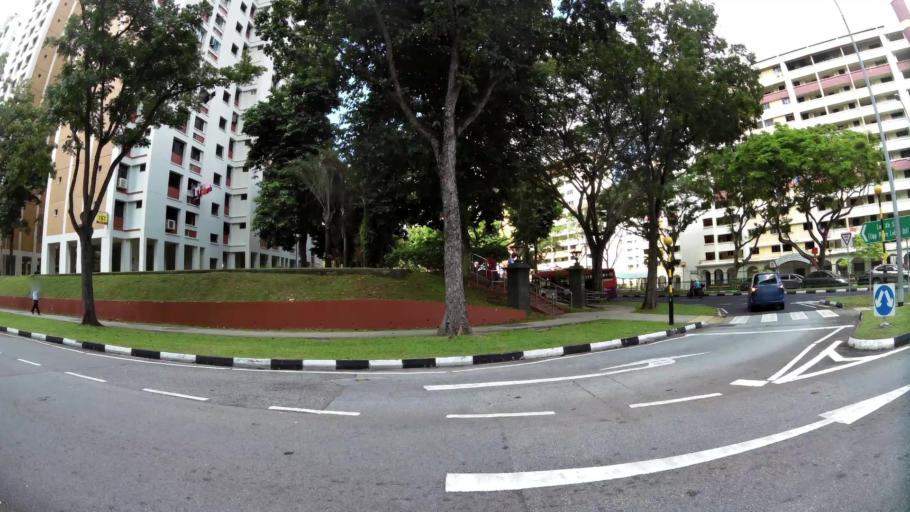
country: SG
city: Singapore
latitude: 1.3523
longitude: 103.8891
